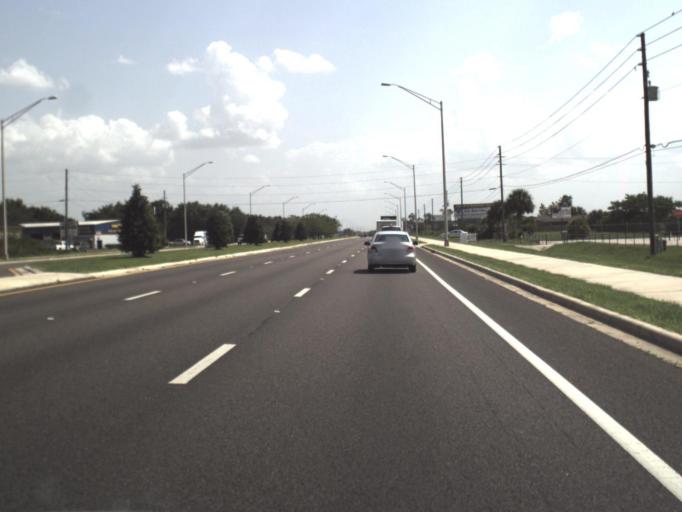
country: US
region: Florida
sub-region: Polk County
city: Lake Hamilton
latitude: 28.0303
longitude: -81.6353
